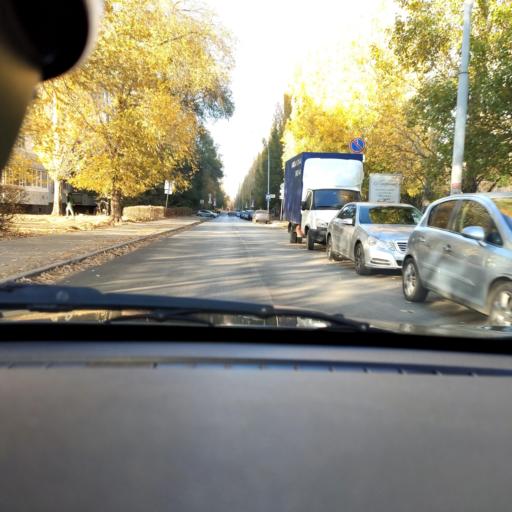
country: RU
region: Samara
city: Tol'yatti
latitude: 53.5216
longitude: 49.3015
